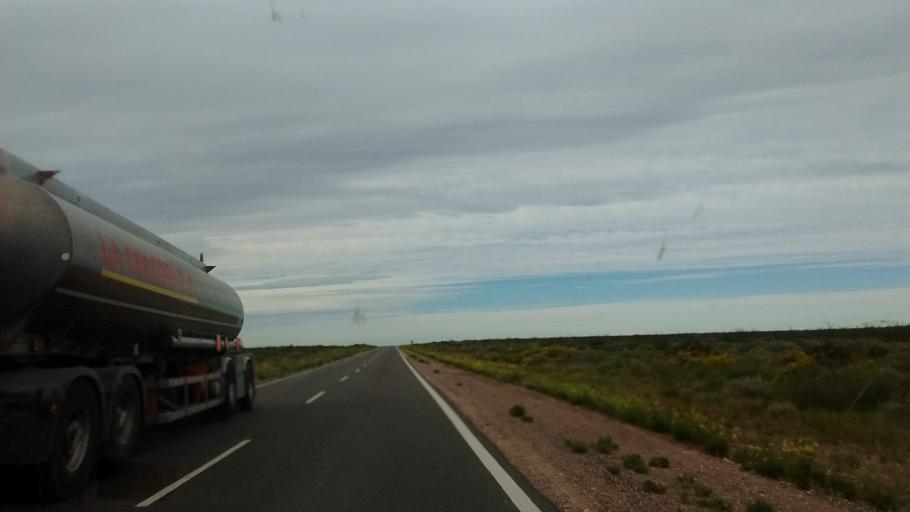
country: AR
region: Rio Negro
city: Contraalmirante Cordero
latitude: -38.3602
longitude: -68.0174
